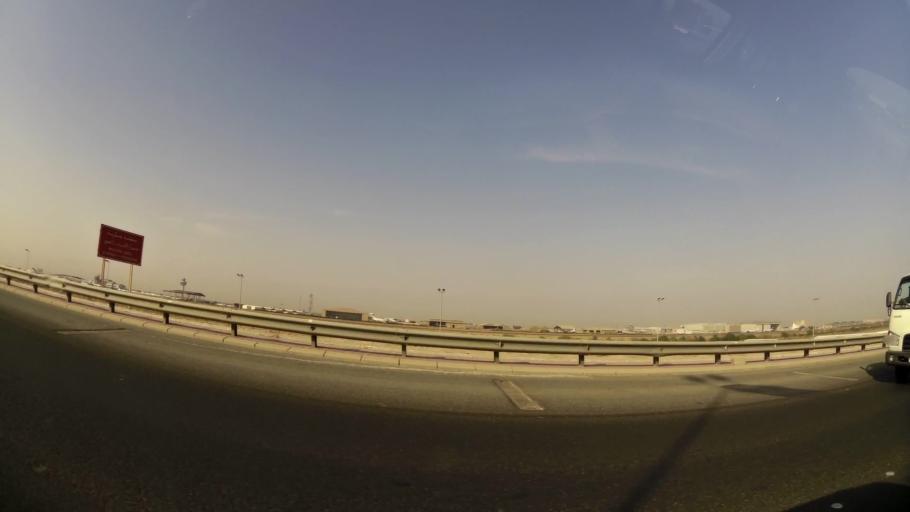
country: KW
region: Al Farwaniyah
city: Janub as Surrah
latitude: 29.2344
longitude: 47.9922
